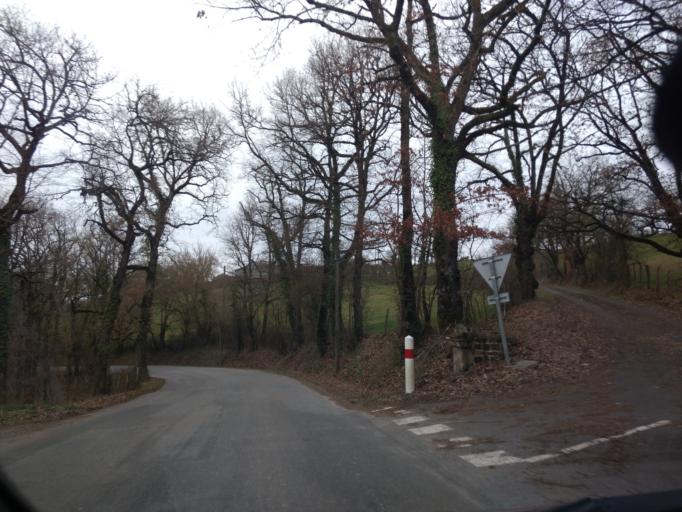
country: FR
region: Midi-Pyrenees
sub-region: Departement de l'Aveyron
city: Saint-Christophe-Vallon
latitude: 44.4624
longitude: 2.4036
